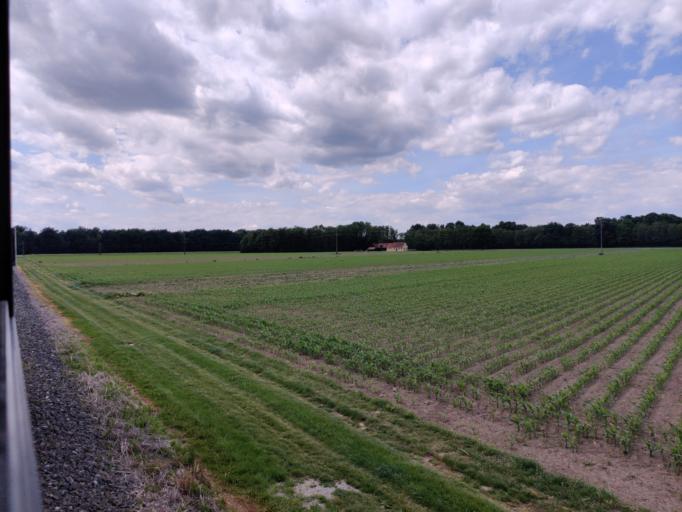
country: AT
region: Styria
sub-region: Politischer Bezirk Suedoststeiermark
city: Eichfeld
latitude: 46.7122
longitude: 15.7496
